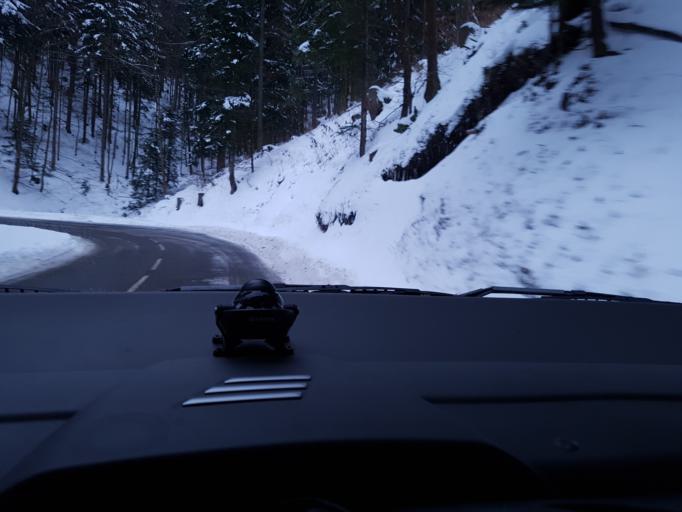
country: FR
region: Alsace
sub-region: Departement du Haut-Rhin
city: Lapoutroie
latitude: 48.2011
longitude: 7.1283
